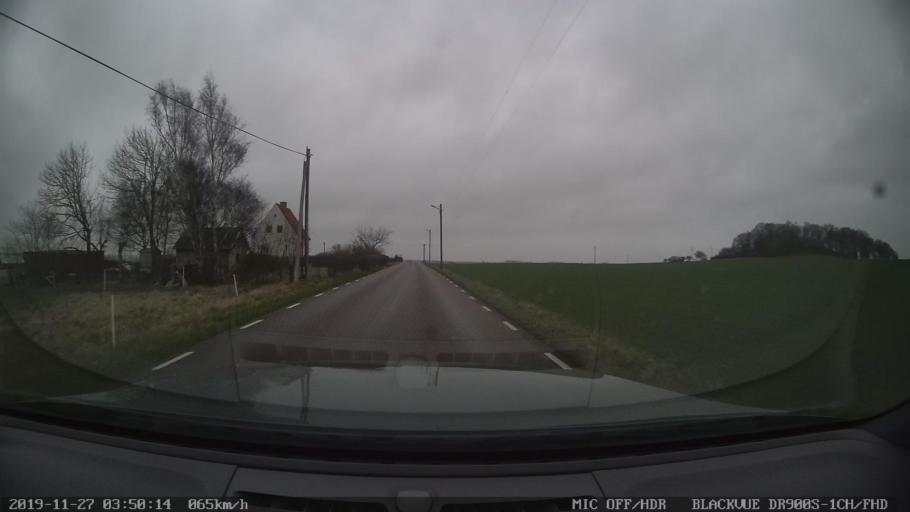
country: SE
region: Skane
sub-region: Hoganas Kommun
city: Hoganas
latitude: 56.2545
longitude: 12.5704
